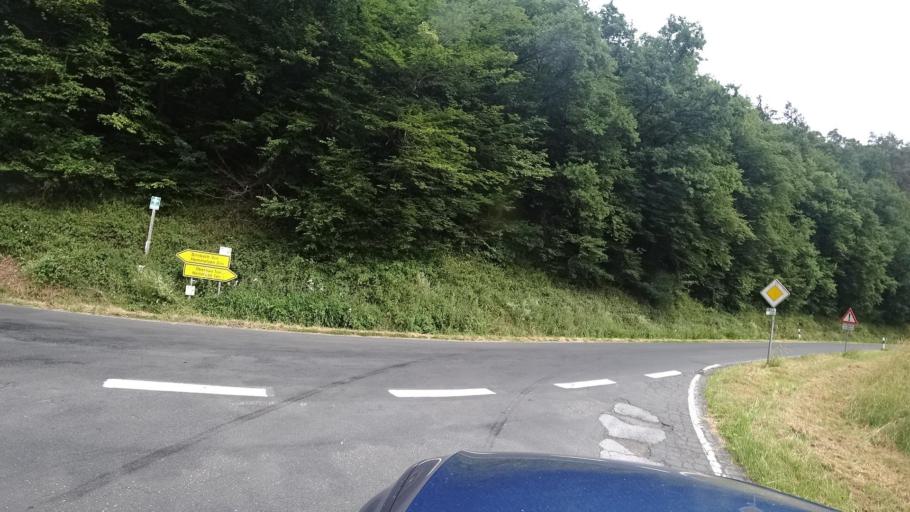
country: DE
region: Rheinland-Pfalz
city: Walterschen
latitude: 50.6788
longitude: 7.5738
